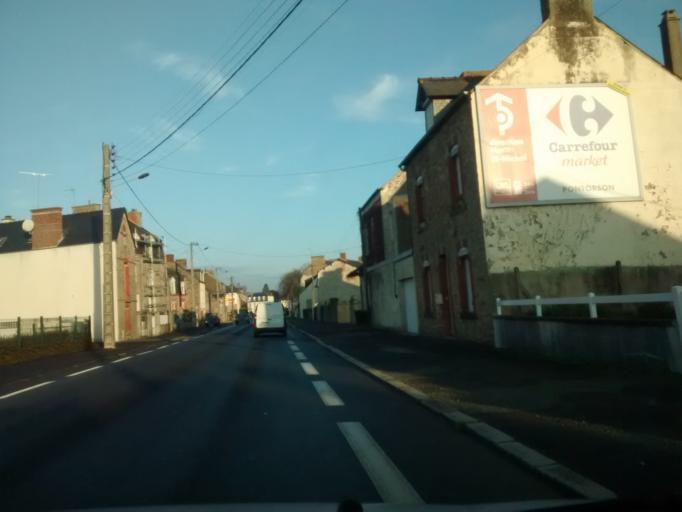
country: FR
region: Lower Normandy
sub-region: Departement de la Manche
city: Pontorson
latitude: 48.5504
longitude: -1.5046
